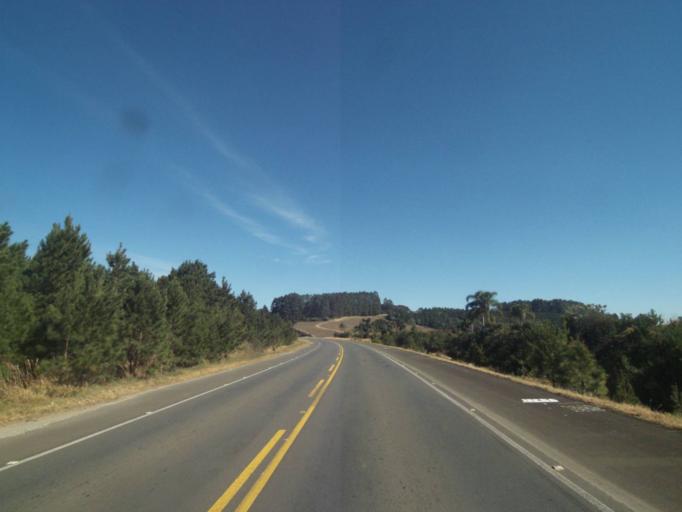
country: BR
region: Parana
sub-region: Tibagi
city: Tibagi
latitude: -24.8085
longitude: -50.4786
